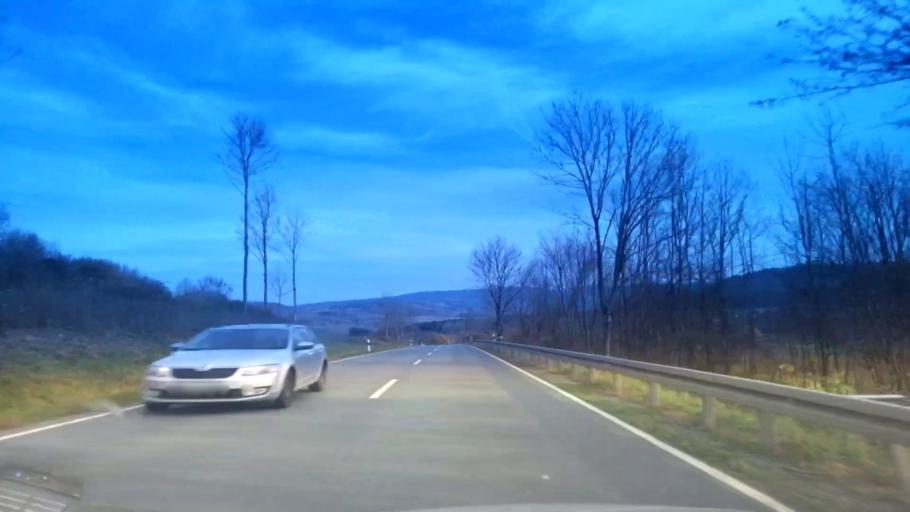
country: DE
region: Bavaria
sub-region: Upper Franconia
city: Neunkirchen am Main
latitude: 49.9619
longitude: 11.6551
